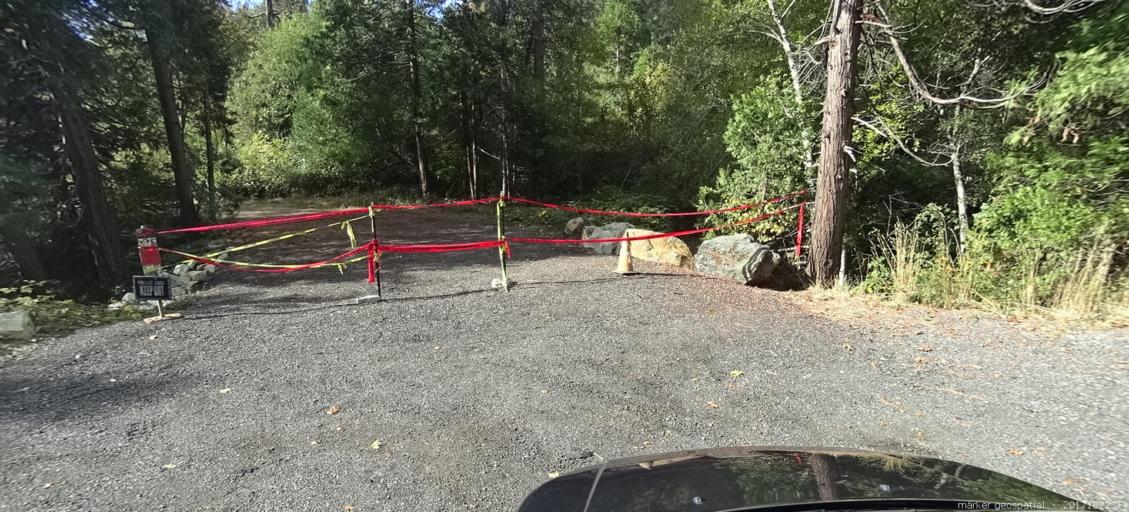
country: US
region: California
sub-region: Siskiyou County
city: Dunsmuir
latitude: 41.0963
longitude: -122.3472
